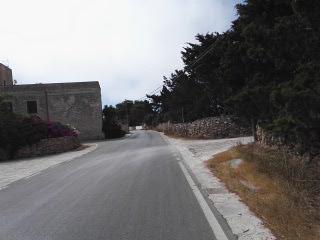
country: IT
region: Sicily
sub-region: Trapani
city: Favignana
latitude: 37.9223
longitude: 12.3415
